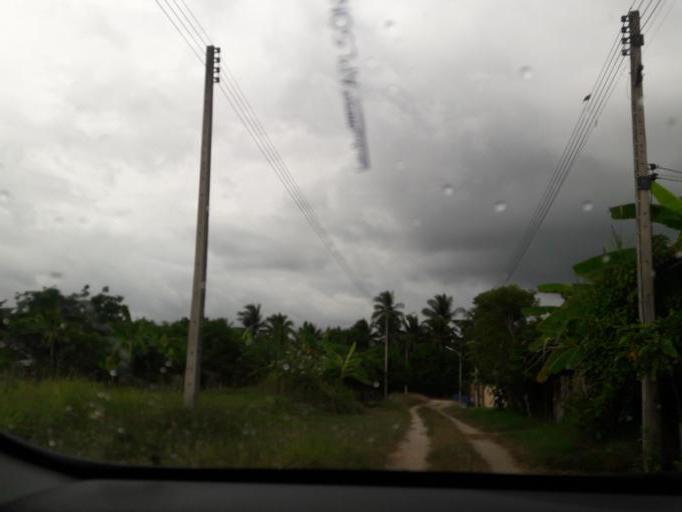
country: TH
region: Ratchaburi
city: Damnoen Saduak
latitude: 13.5666
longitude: 99.9762
